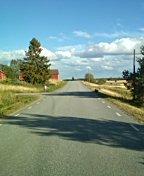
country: SE
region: Uppsala
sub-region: Enkopings Kommun
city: Grillby
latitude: 59.6697
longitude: 17.2263
